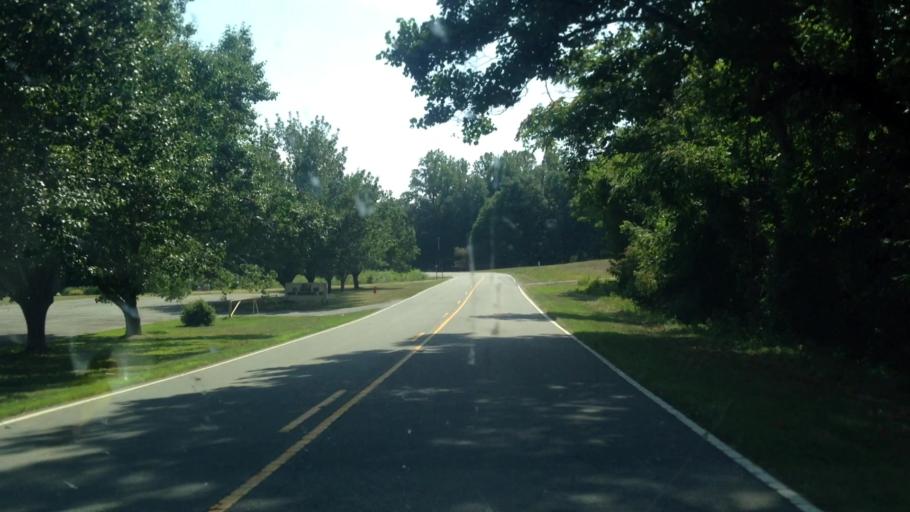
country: US
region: North Carolina
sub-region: Stokes County
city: Walnut Cove
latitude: 36.3008
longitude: -80.0590
